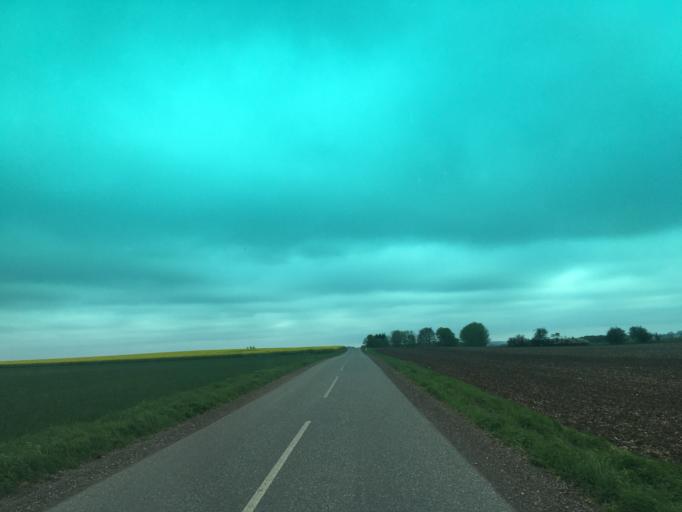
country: DK
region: Zealand
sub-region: Ringsted Kommune
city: Ringsted
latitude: 55.4287
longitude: 11.7134
